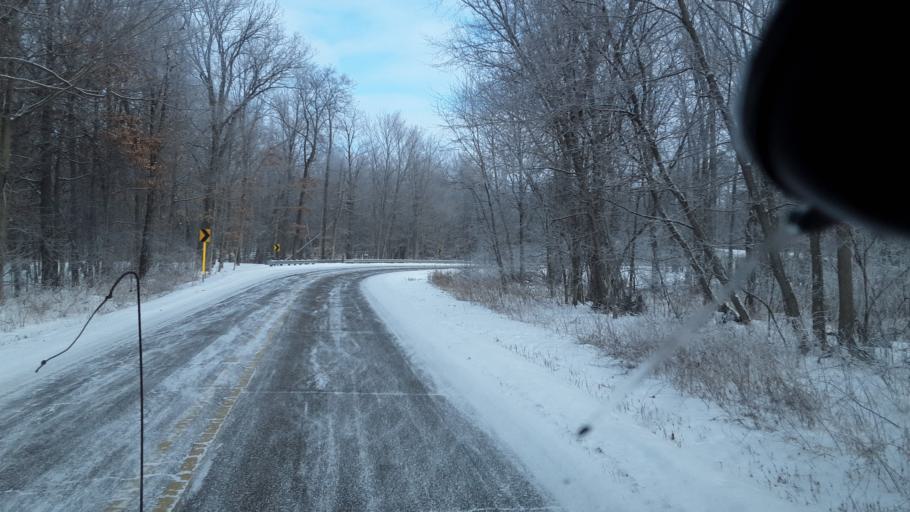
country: US
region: Michigan
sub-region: Ingham County
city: Leslie
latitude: 42.3927
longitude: -84.4924
